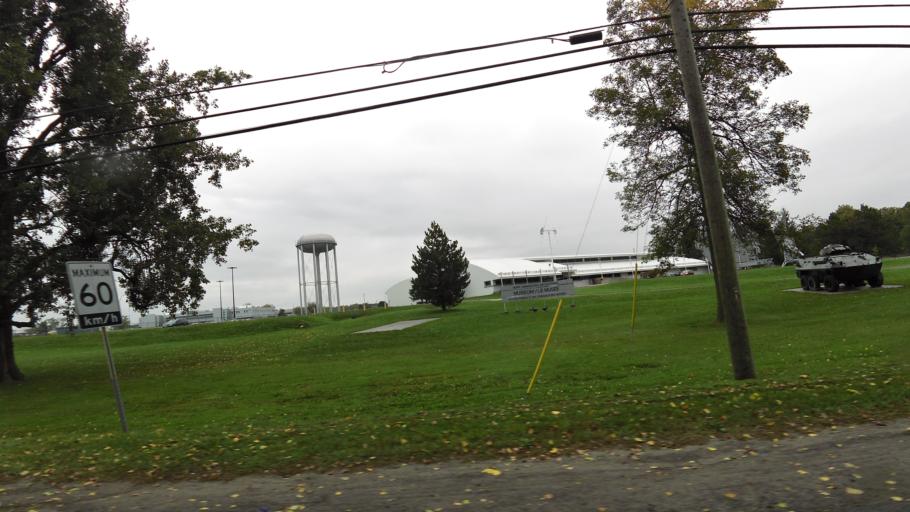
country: CA
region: Ontario
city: Kingston
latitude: 44.2410
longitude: -76.4398
